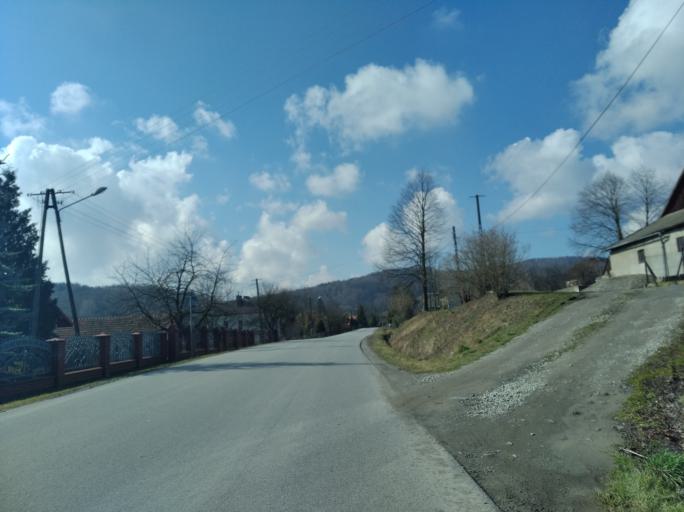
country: PL
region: Subcarpathian Voivodeship
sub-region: Powiat strzyzowski
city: Frysztak
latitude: 49.8732
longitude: 21.5714
